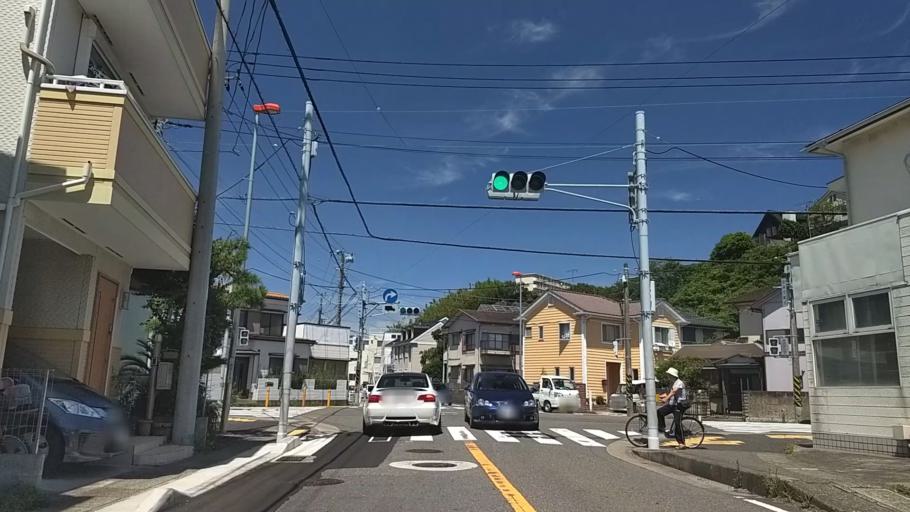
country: JP
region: Kanagawa
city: Zushi
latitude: 35.3024
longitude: 139.5913
